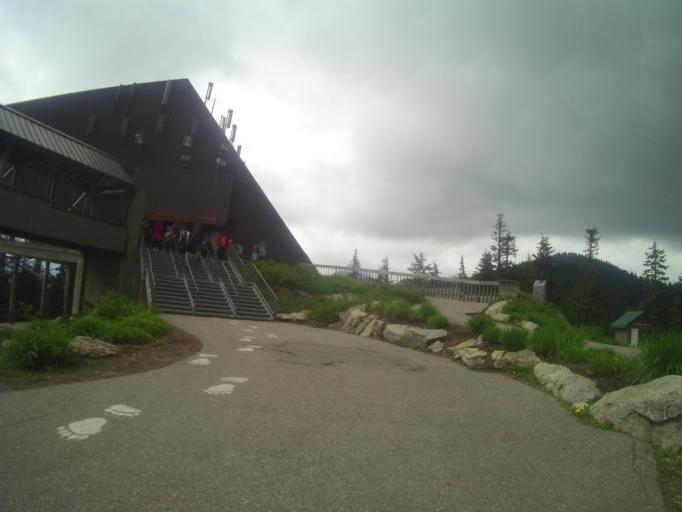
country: CA
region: British Columbia
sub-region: Fraser Valley Regional District
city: North Vancouver
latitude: 49.3793
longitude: -123.0830
